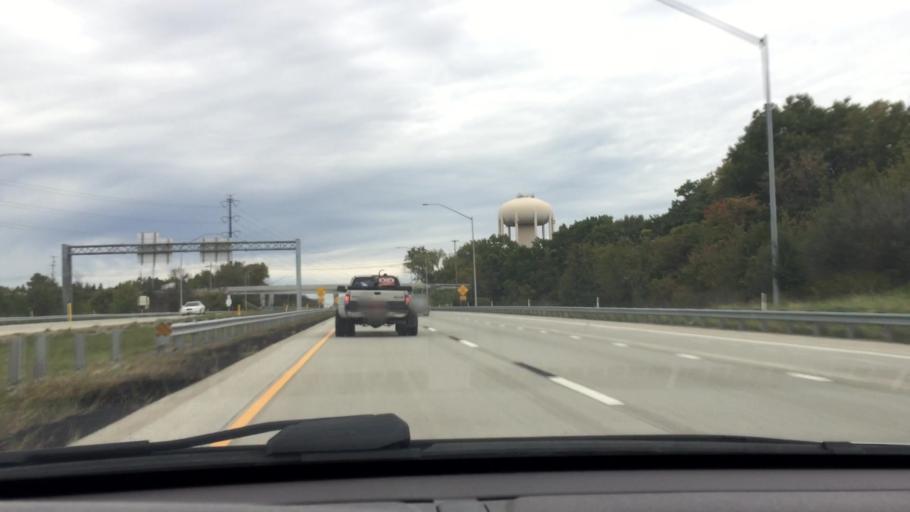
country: US
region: Pennsylvania
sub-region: Allegheny County
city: Carnot-Moon
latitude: 40.5298
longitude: -80.2723
